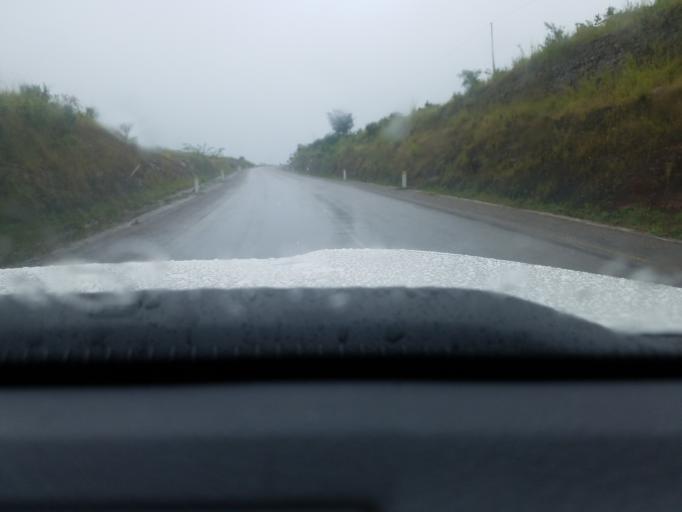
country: TZ
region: Kigoma
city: Mwandiga
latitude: -4.6595
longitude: 29.7231
